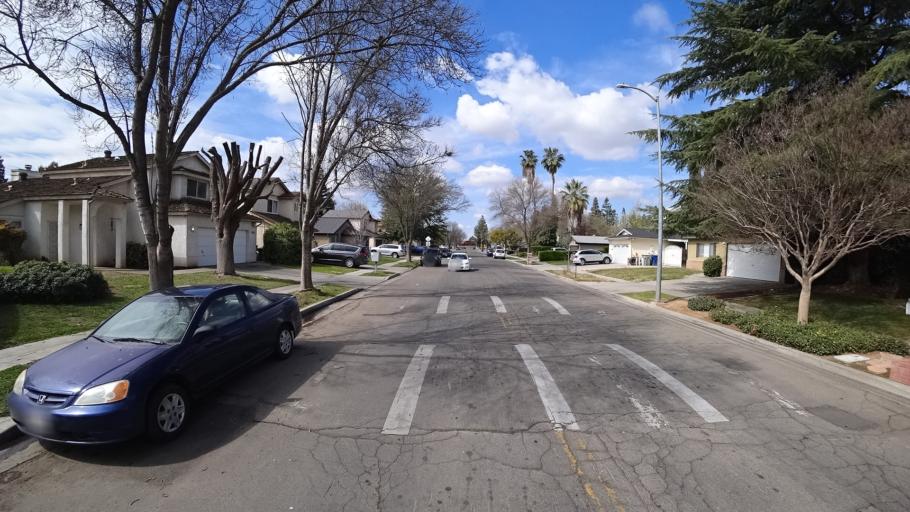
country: US
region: California
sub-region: Fresno County
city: Fresno
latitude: 36.8191
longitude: -119.8542
